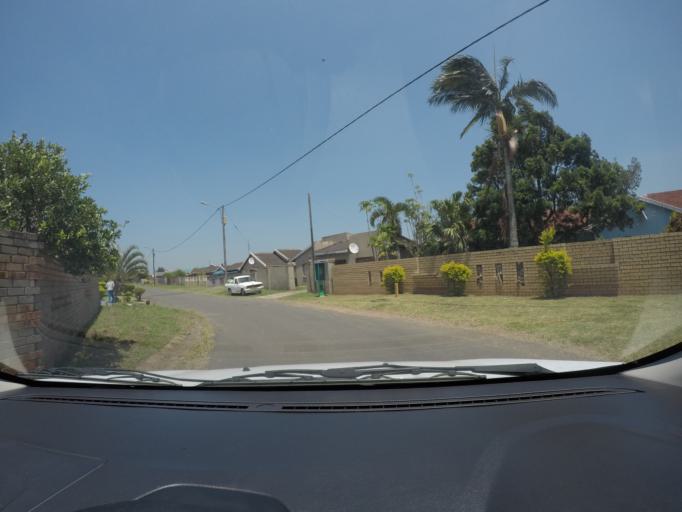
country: ZA
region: KwaZulu-Natal
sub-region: uThungulu District Municipality
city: eSikhawini
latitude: -28.8695
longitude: 31.9122
